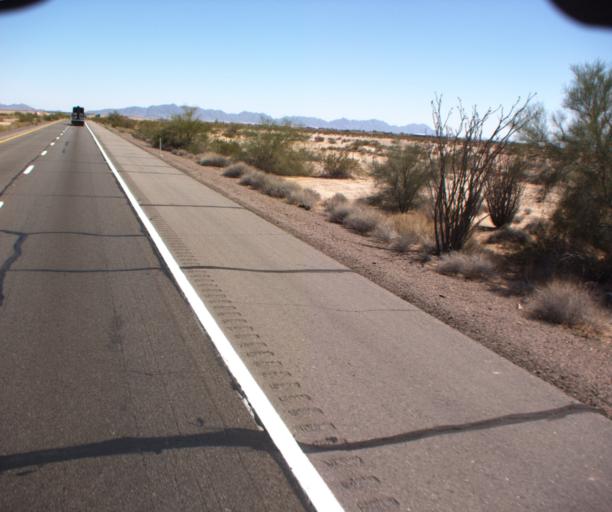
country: US
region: Arizona
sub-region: Yuma County
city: Wellton
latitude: 32.6915
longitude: -113.9656
